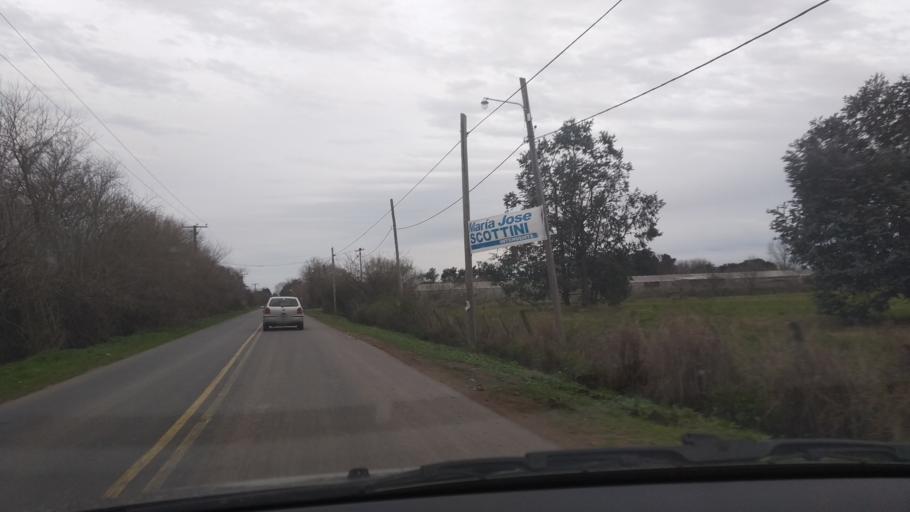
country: AR
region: Buenos Aires
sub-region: Partido de La Plata
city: La Plata
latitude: -35.0011
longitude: -58.0664
